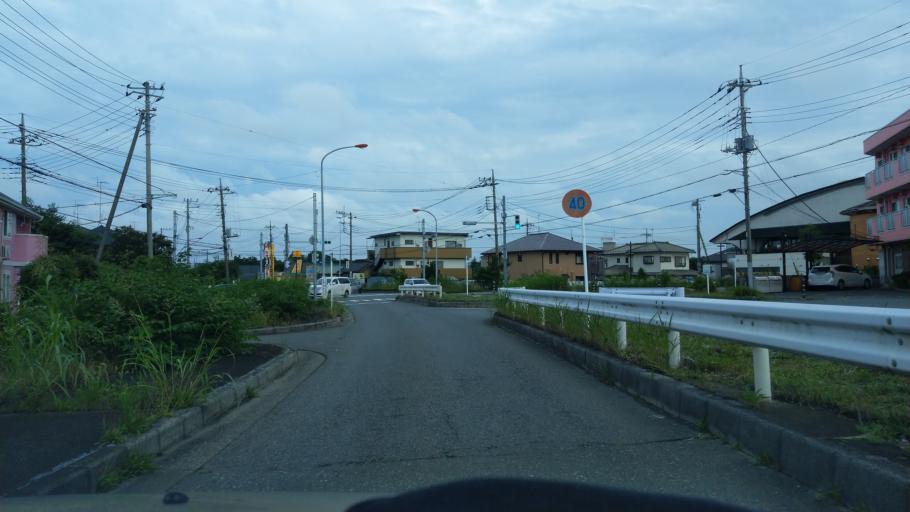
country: JP
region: Saitama
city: Kamifukuoka
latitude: 35.9159
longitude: 139.5579
